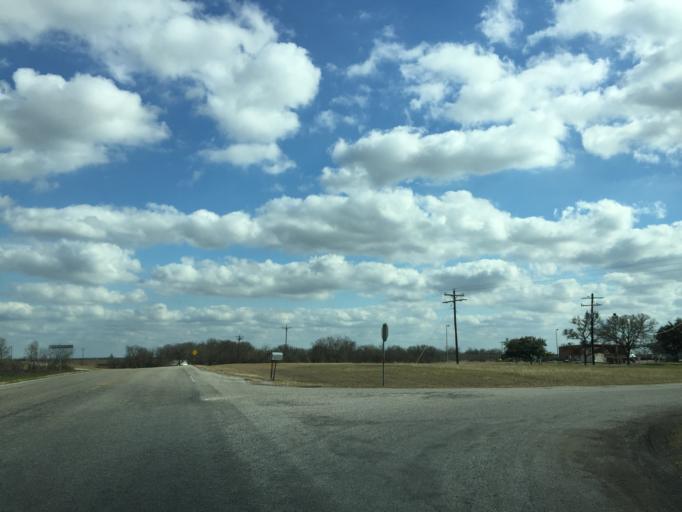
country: US
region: Texas
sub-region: Williamson County
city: Granger
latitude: 30.7197
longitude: -97.3212
